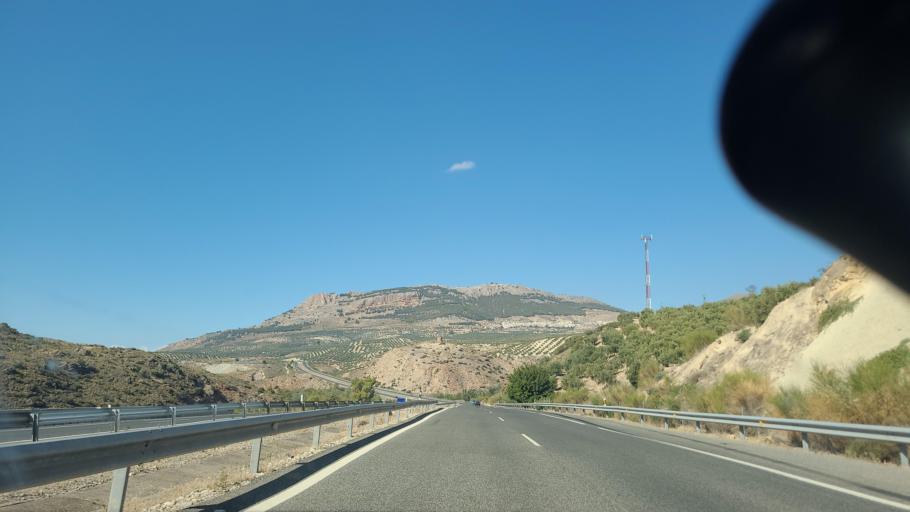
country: ES
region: Andalusia
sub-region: Provincia de Jaen
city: Pegalajar
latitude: 37.7049
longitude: -3.6370
